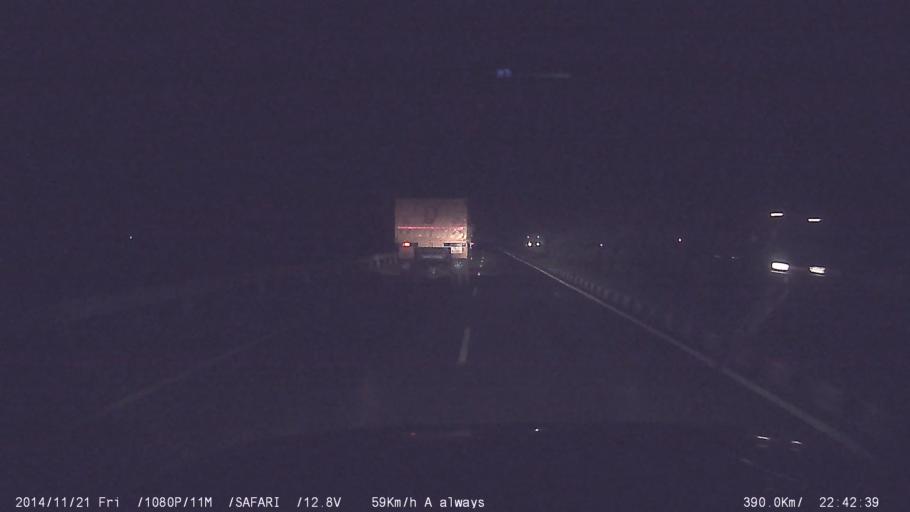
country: IN
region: Tamil Nadu
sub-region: Villupuram
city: Tindivanam
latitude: 12.2378
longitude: 79.6630
